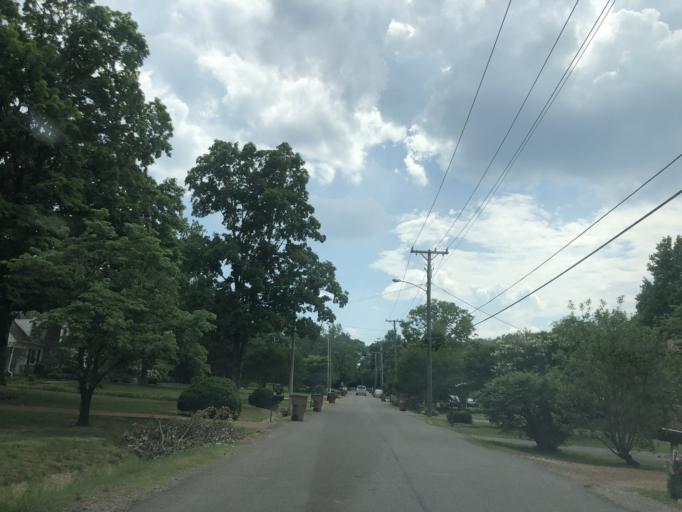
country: US
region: Tennessee
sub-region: Davidson County
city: Belle Meade
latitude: 36.1225
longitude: -86.8196
